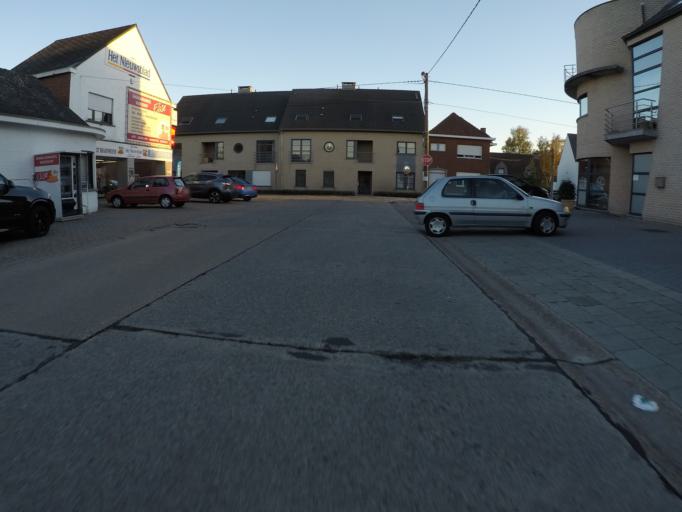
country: BE
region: Flanders
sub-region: Provincie Vlaams-Brabant
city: Begijnendijk
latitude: 51.0186
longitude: 4.7854
